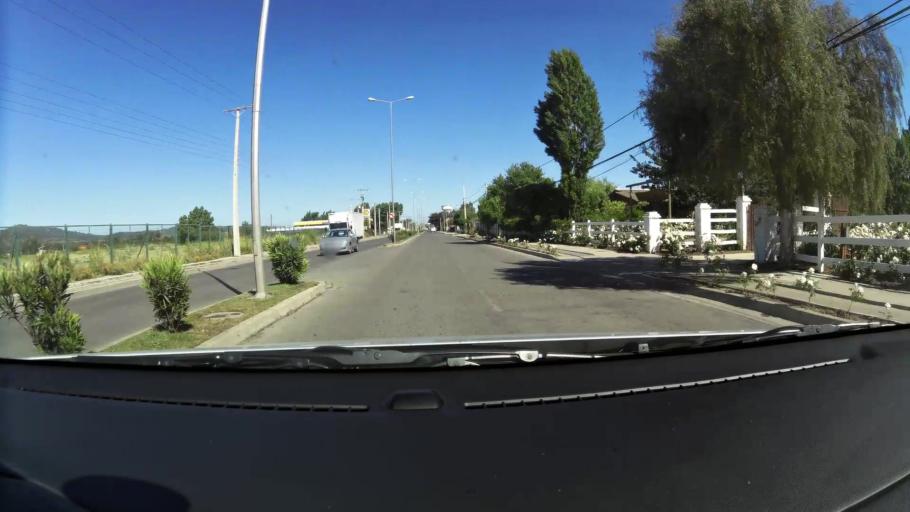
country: CL
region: Valparaiso
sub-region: Provincia de Marga Marga
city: Quilpue
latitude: -33.3277
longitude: -71.3951
